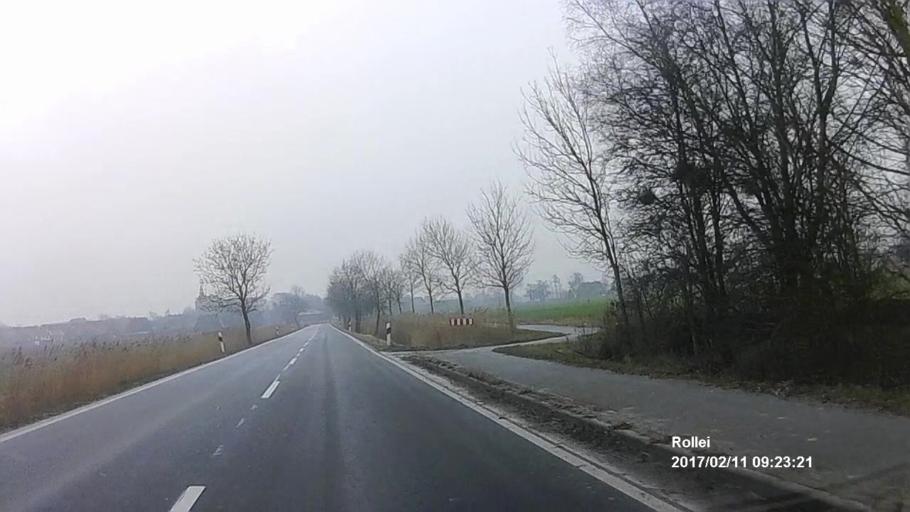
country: DE
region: Lower Saxony
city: Wirdum
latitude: 53.4782
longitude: 7.1380
